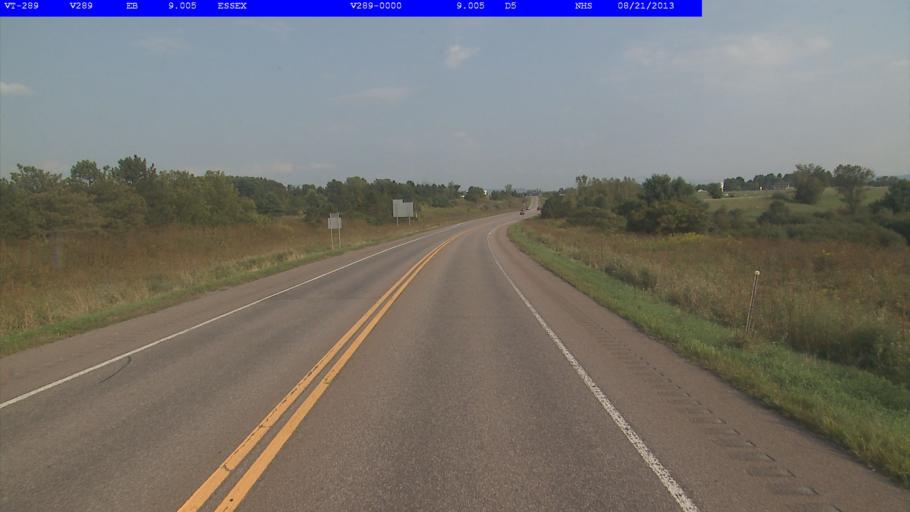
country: US
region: Vermont
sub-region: Chittenden County
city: Essex Junction
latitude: 44.5118
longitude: -73.0948
